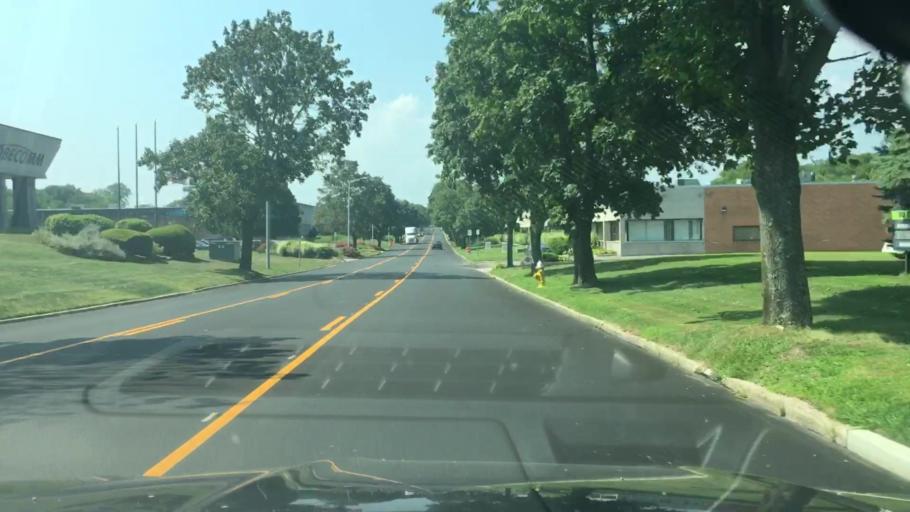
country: US
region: New York
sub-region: Suffolk County
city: Hauppauge
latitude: 40.8160
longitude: -73.2369
